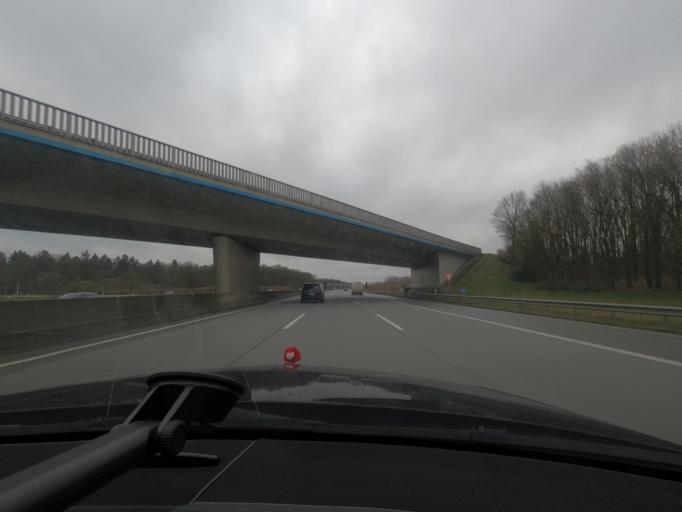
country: DE
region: Schleswig-Holstein
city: Grossenaspe
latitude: 54.0022
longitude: 9.9341
